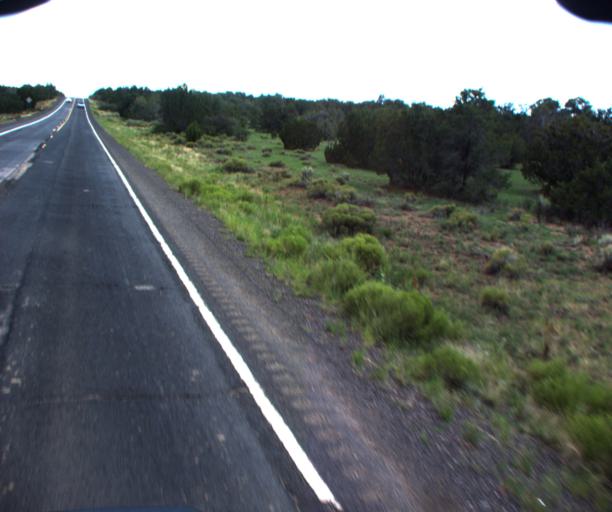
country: US
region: Arizona
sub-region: Coconino County
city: Williams
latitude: 35.4392
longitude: -112.1715
